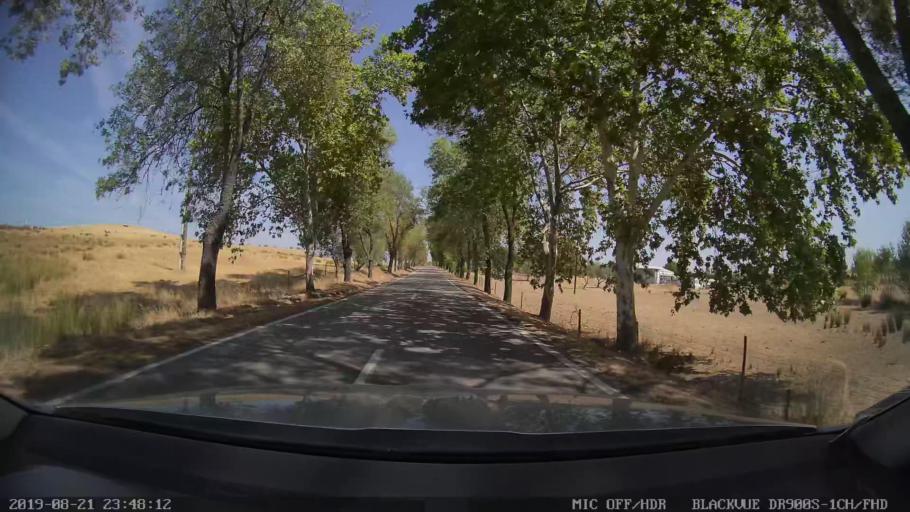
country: PT
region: Castelo Branco
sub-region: Idanha-A-Nova
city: Idanha-a-Nova
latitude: 39.8616
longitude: -7.2584
